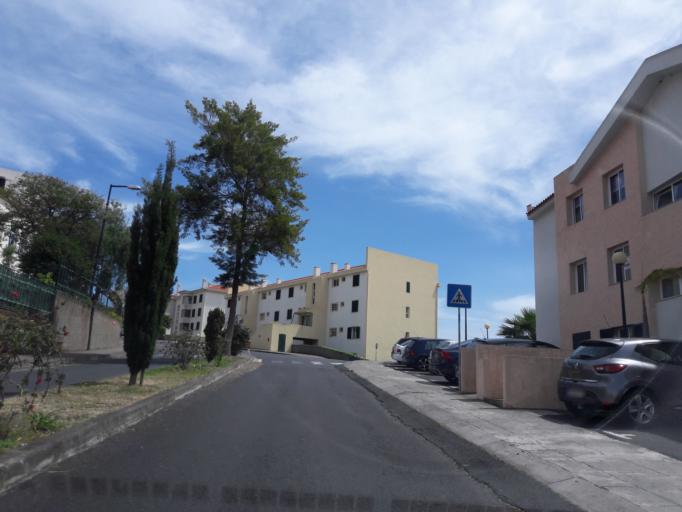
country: PT
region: Madeira
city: Canico
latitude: 32.6531
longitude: -16.8541
